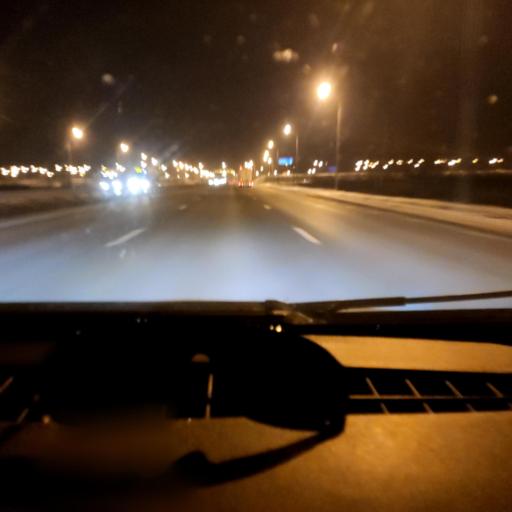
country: RU
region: Bashkortostan
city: Kabakovo
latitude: 54.6509
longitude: 56.0746
